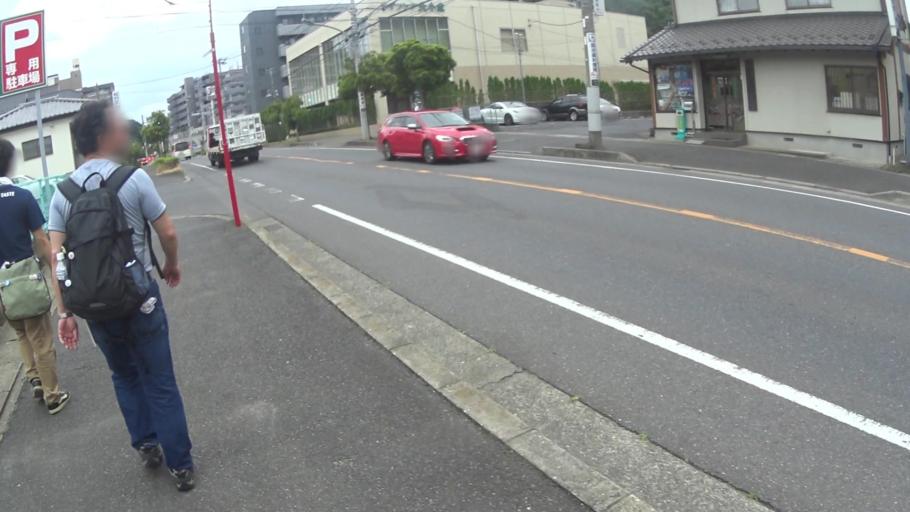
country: JP
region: Chiba
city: Nagareyama
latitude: 35.8367
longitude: 139.9255
